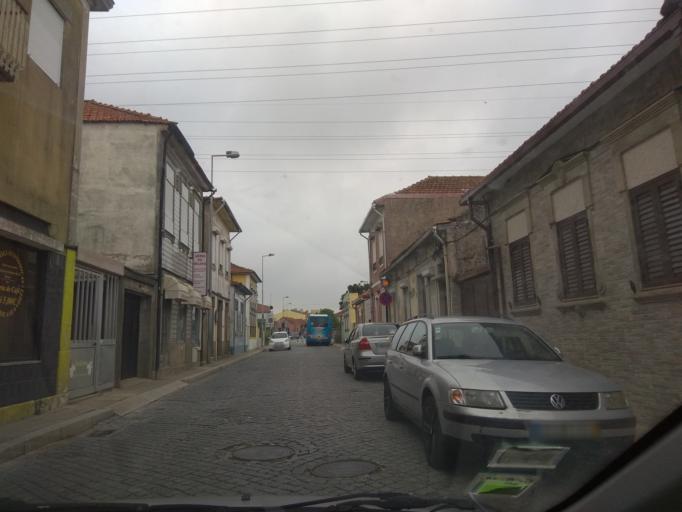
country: PT
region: Porto
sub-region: Matosinhos
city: Guifoes
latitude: 41.1953
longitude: -8.6621
